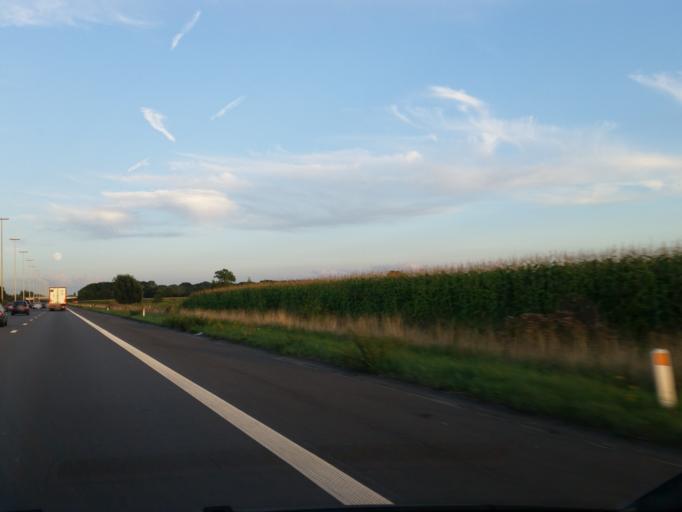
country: BE
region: Flanders
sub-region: Provincie West-Vlaanderen
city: Oostkamp
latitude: 51.1370
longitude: 3.2670
